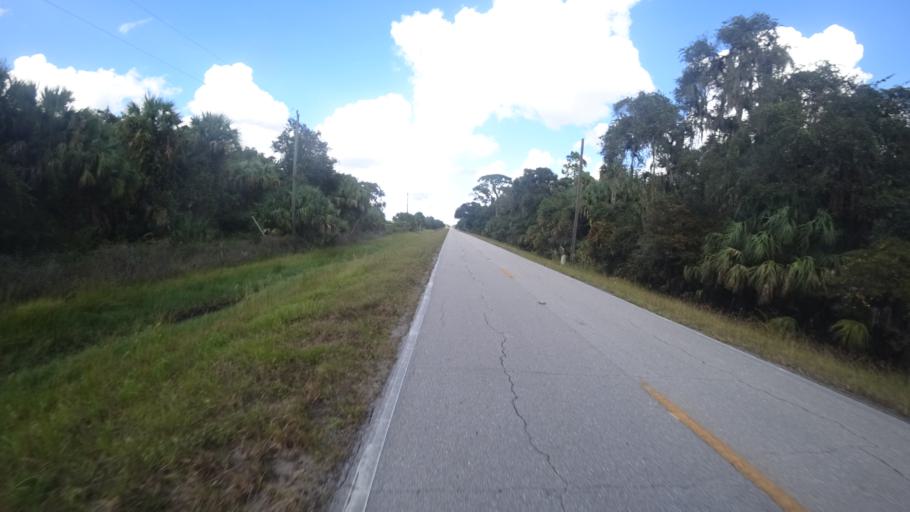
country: US
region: Florida
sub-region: Sarasota County
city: North Port
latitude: 27.2220
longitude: -82.1221
